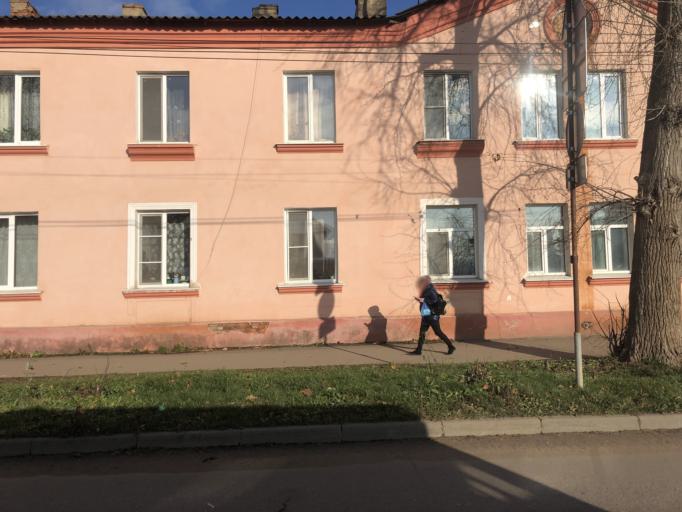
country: RU
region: Tverskaya
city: Rzhev
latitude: 56.2630
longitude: 34.3249
